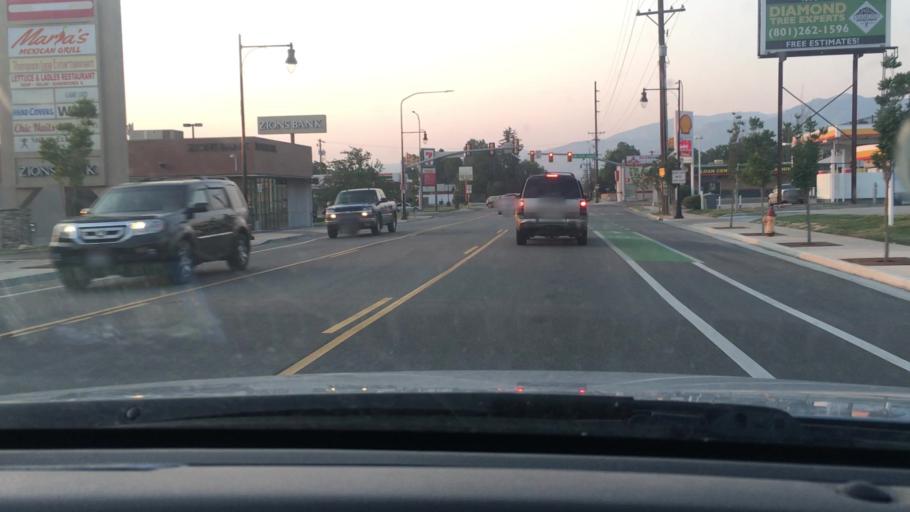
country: US
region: Utah
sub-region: Salt Lake County
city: Canyon Rim
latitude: 40.6990
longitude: -111.8244
